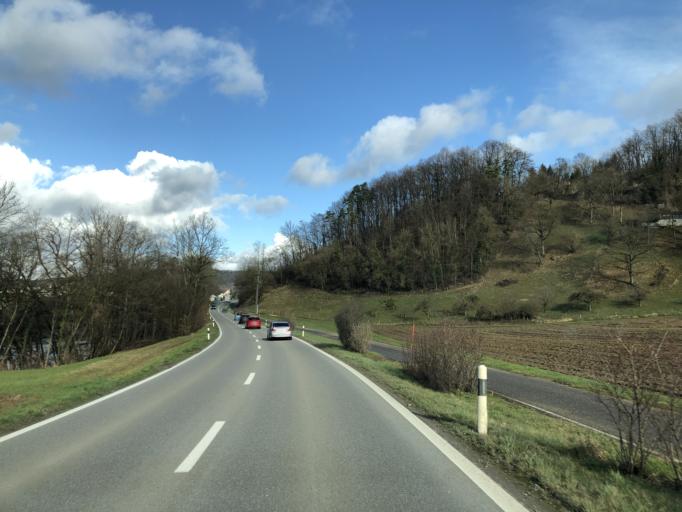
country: CH
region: Aargau
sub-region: Bezirk Baden
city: Gebenstorf
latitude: 47.4714
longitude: 8.2346
